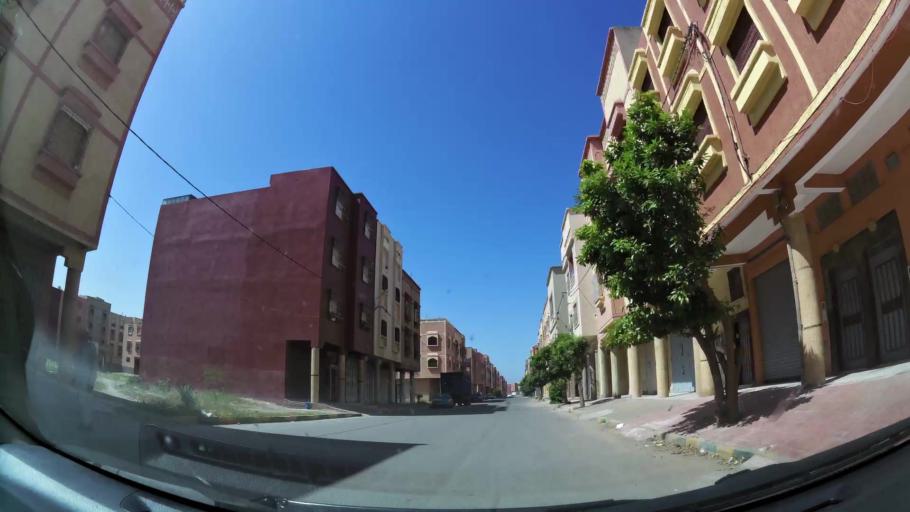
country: MA
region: Souss-Massa-Draa
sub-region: Inezgane-Ait Mellou
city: Inezgane
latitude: 30.3319
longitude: -9.5059
